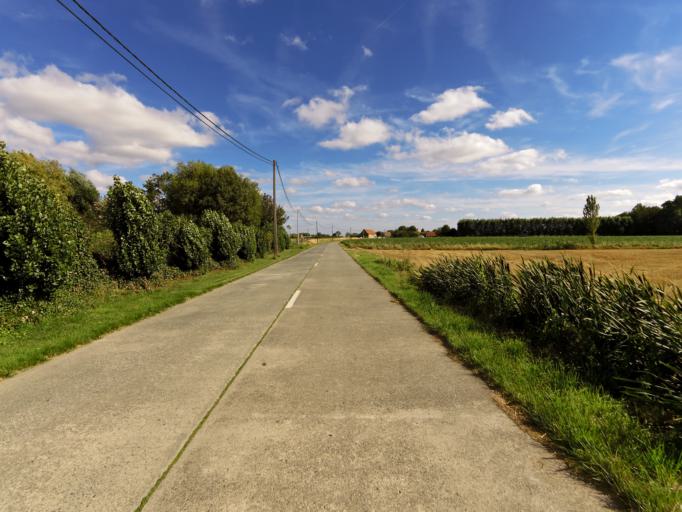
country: BE
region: Flanders
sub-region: Provincie West-Vlaanderen
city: Alveringem
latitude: 50.9736
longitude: 2.6639
